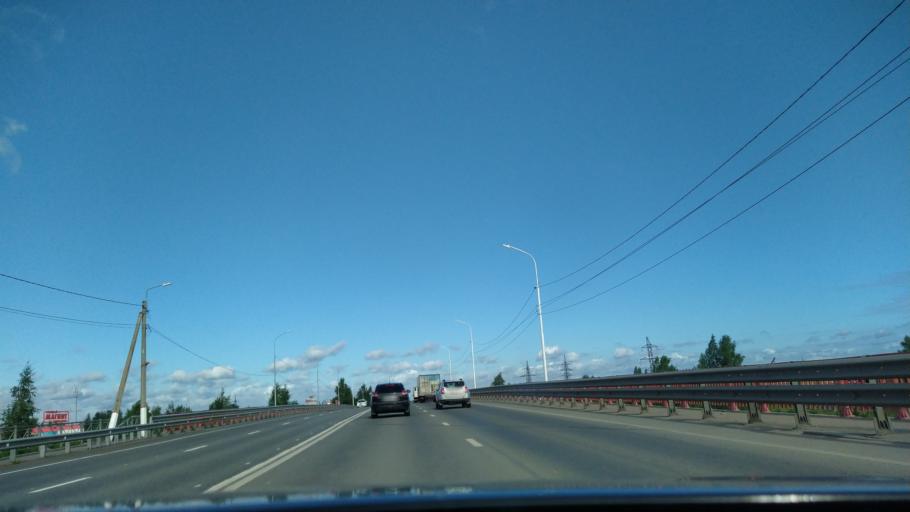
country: RU
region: Leningrad
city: Tosno
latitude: 59.5507
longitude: 30.8594
